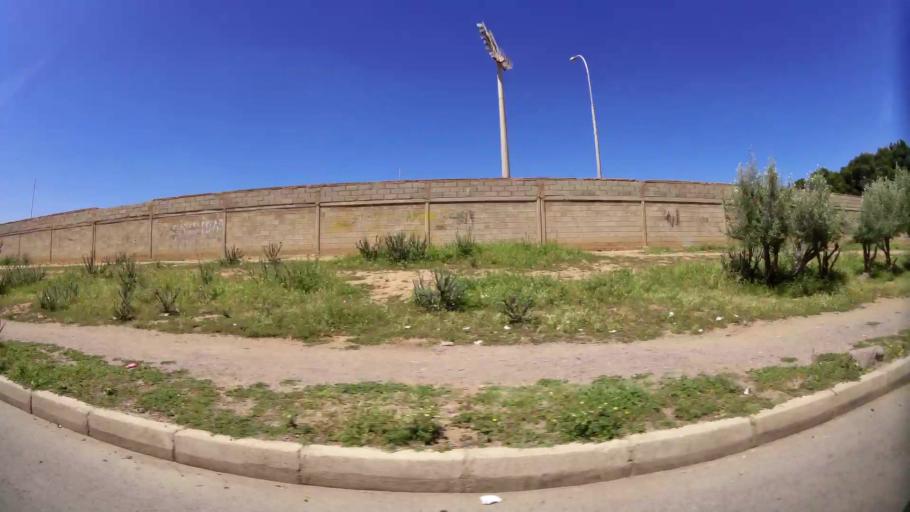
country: MA
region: Oriental
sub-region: Oujda-Angad
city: Oujda
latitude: 34.6606
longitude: -1.9337
